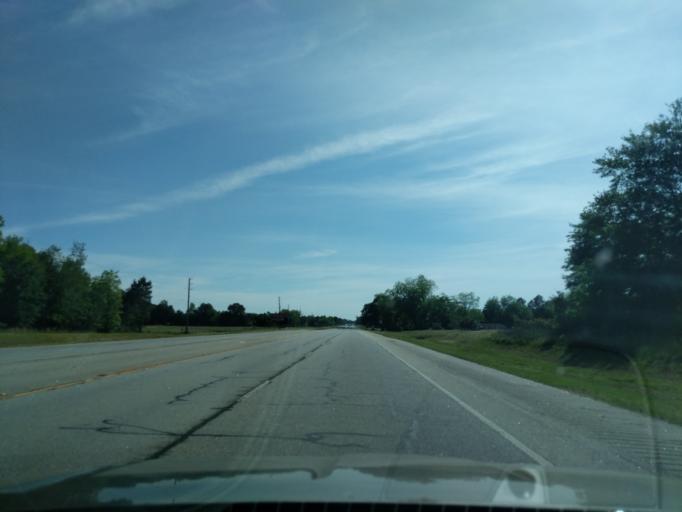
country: US
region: Georgia
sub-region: Jefferson County
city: Wrens
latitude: 33.2299
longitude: -82.3578
